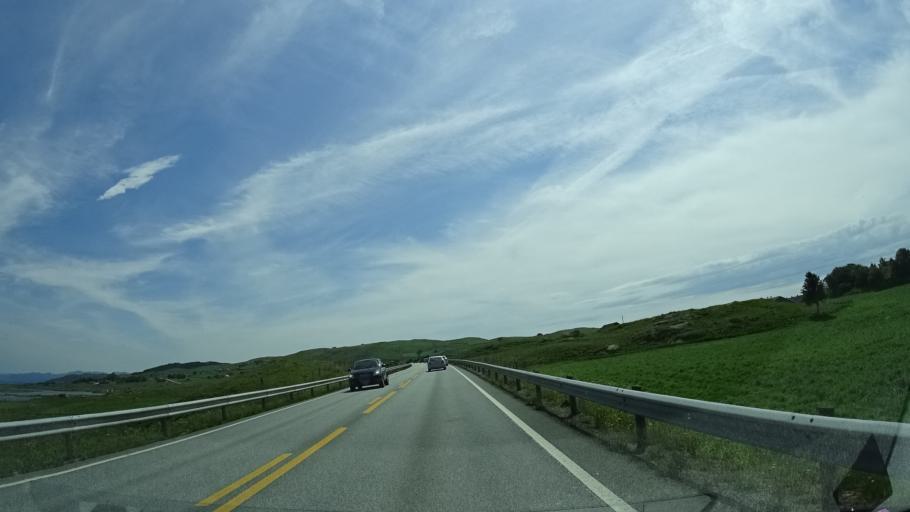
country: NO
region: Rogaland
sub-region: Rennesoy
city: Vikevag
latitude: 59.1323
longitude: 5.6080
